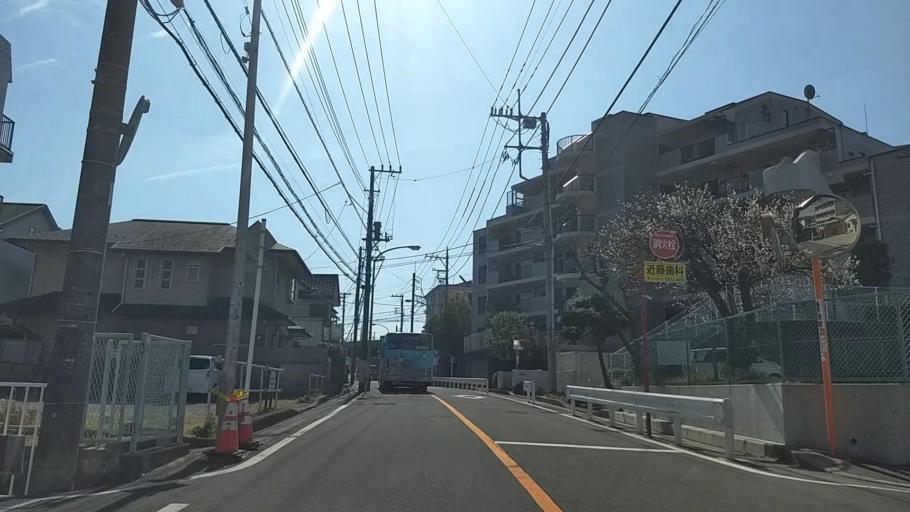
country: JP
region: Kanagawa
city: Kamakura
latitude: 35.3694
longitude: 139.5385
